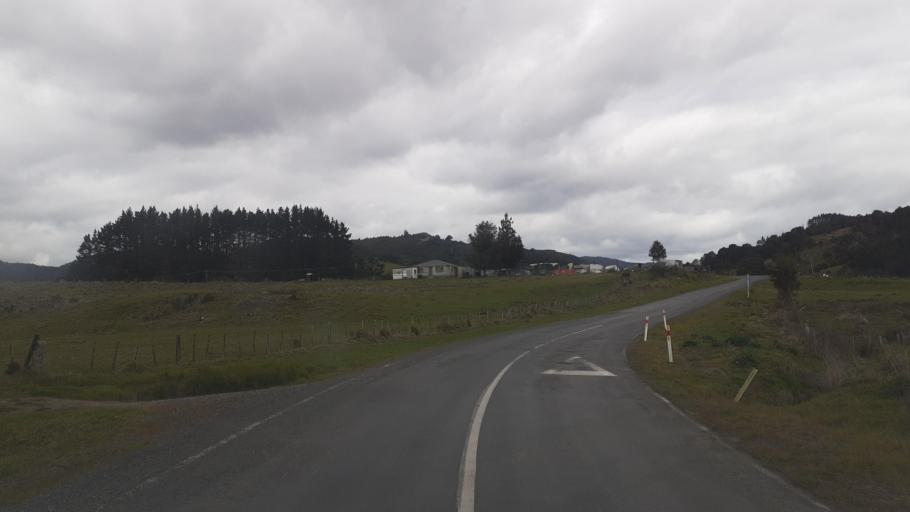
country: NZ
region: Northland
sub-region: Far North District
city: Moerewa
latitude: -35.5856
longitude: 173.9743
